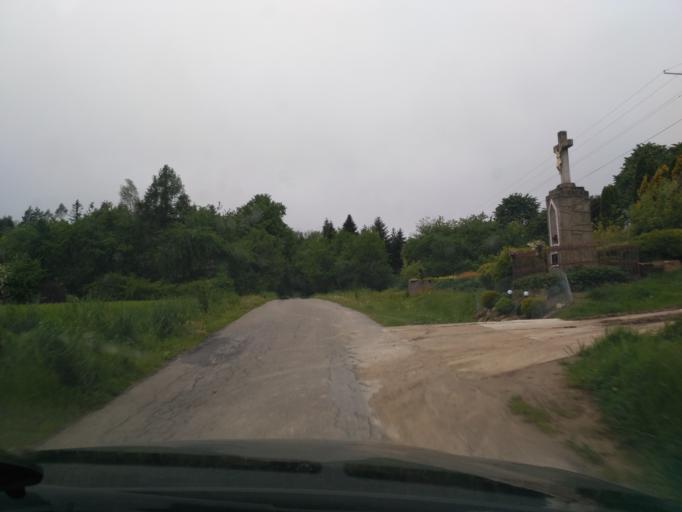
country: PL
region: Subcarpathian Voivodeship
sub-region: Powiat debicki
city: Jodlowa
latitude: 49.8571
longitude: 21.2422
